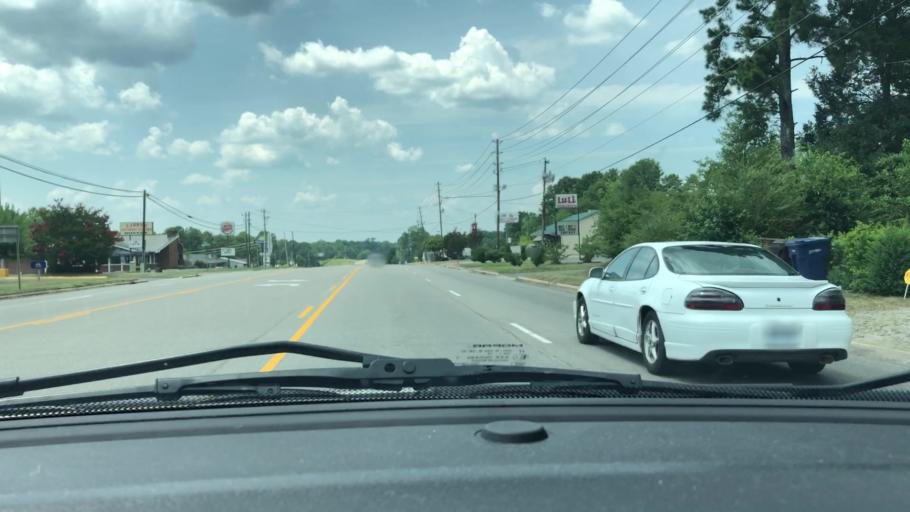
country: US
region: North Carolina
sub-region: Lee County
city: Sanford
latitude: 35.4965
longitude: -79.1970
